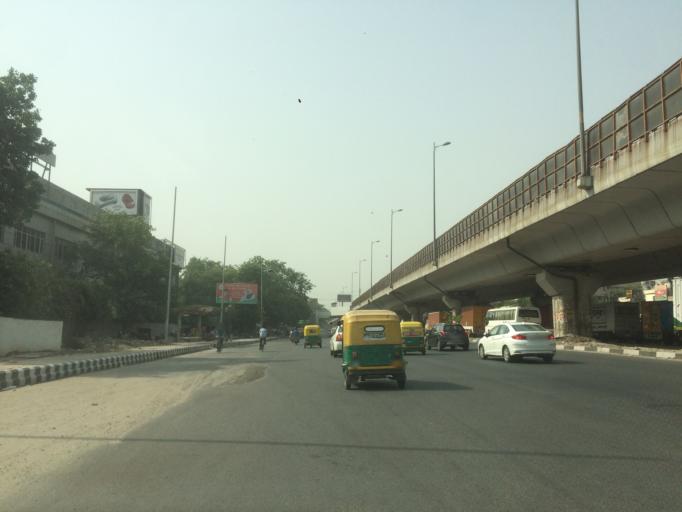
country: IN
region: NCT
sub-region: Central Delhi
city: Karol Bagh
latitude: 28.6279
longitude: 77.1339
